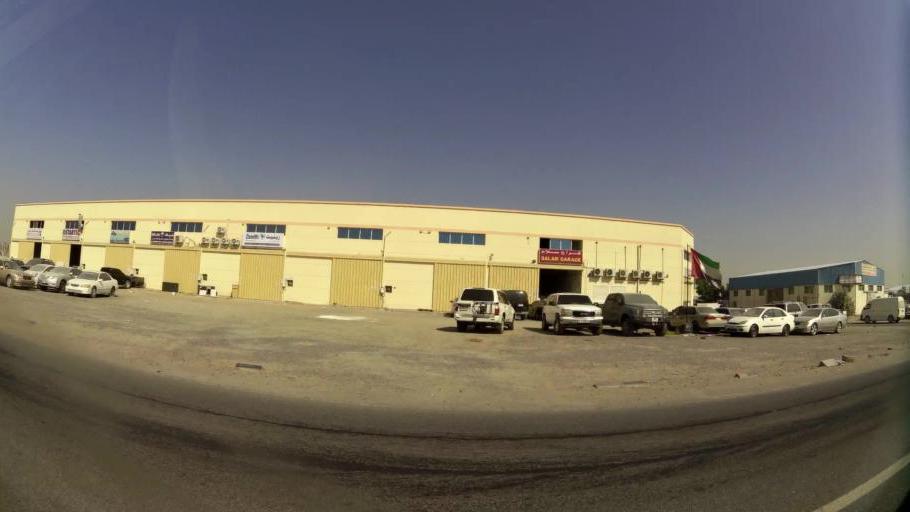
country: AE
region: Ajman
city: Ajman
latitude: 25.4323
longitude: 55.5361
